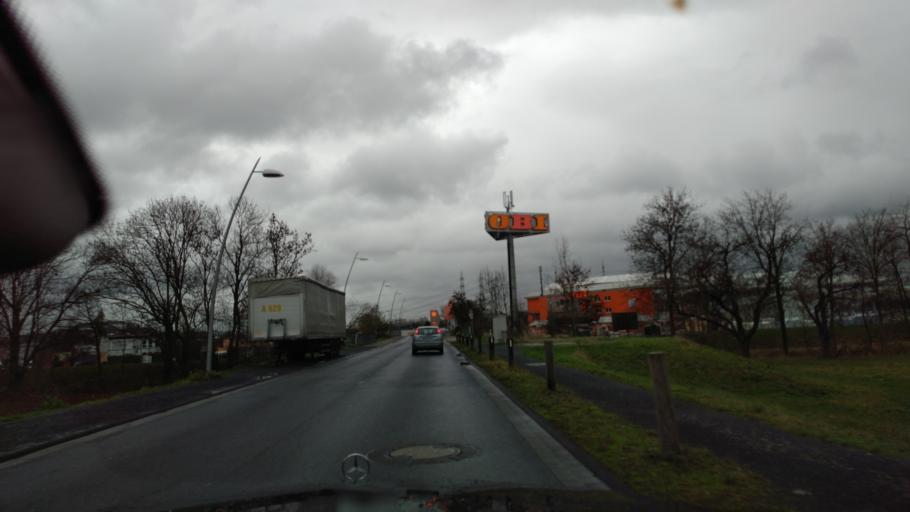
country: DE
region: North Rhine-Westphalia
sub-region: Regierungsbezirk Koln
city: Siegburg
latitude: 50.8007
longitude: 7.1846
